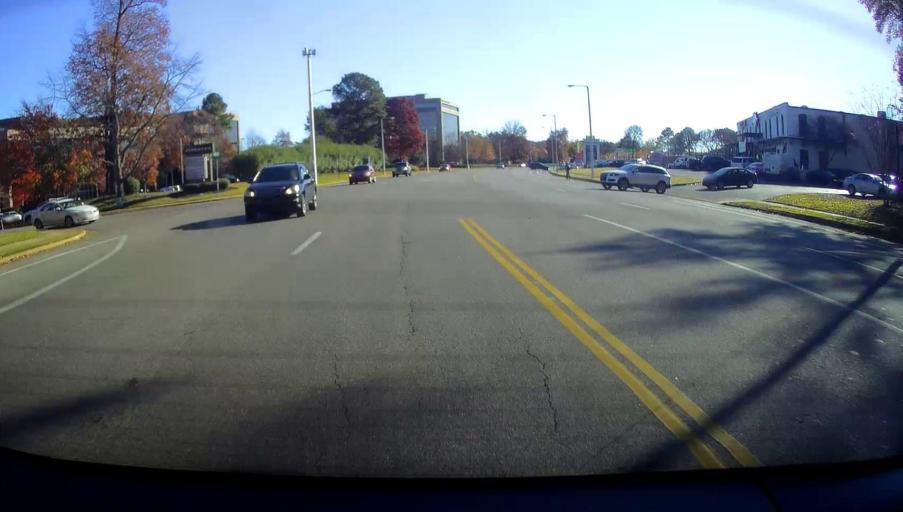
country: US
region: Tennessee
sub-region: Shelby County
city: Germantown
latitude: 35.1014
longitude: -89.8394
